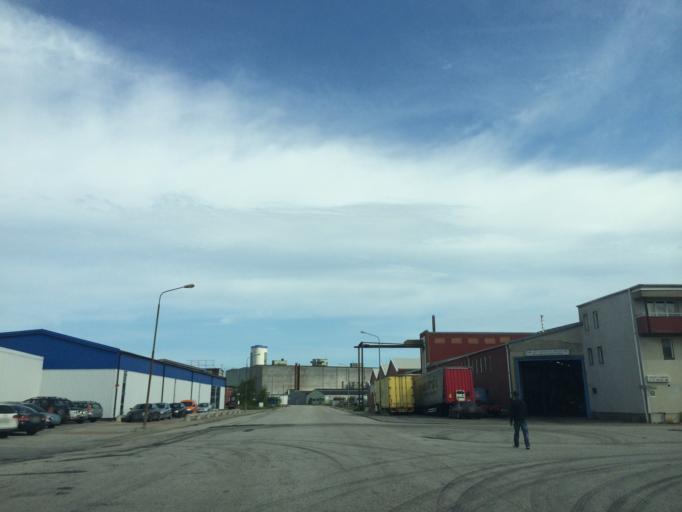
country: SE
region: Skane
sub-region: Malmo
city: Malmoe
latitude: 55.6182
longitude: 13.0199
